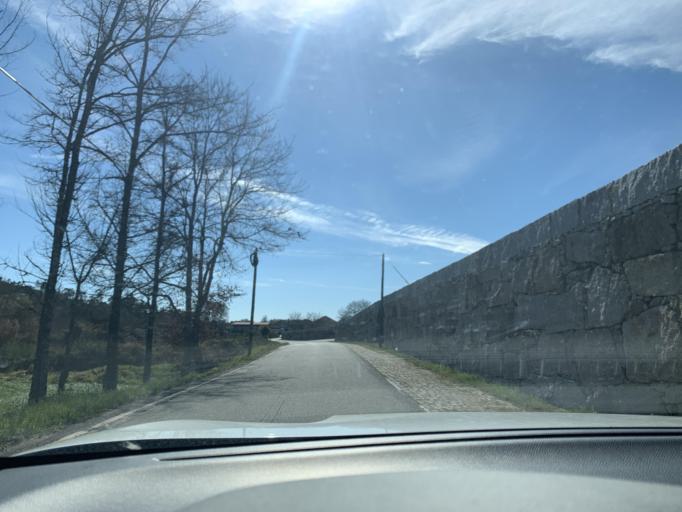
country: PT
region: Viseu
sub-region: Concelho de Tondela
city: Tondela
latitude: 40.5951
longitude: -8.0243
